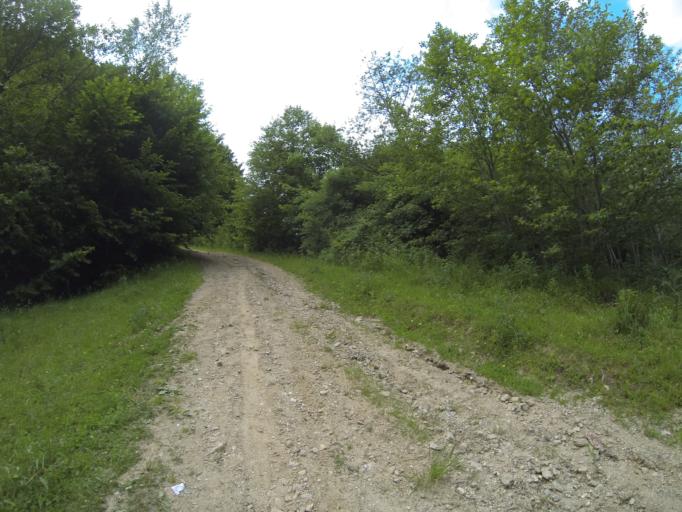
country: RO
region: Brasov
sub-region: Comuna Poiana Marului
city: Poiana Marului
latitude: 45.6507
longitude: 25.2927
